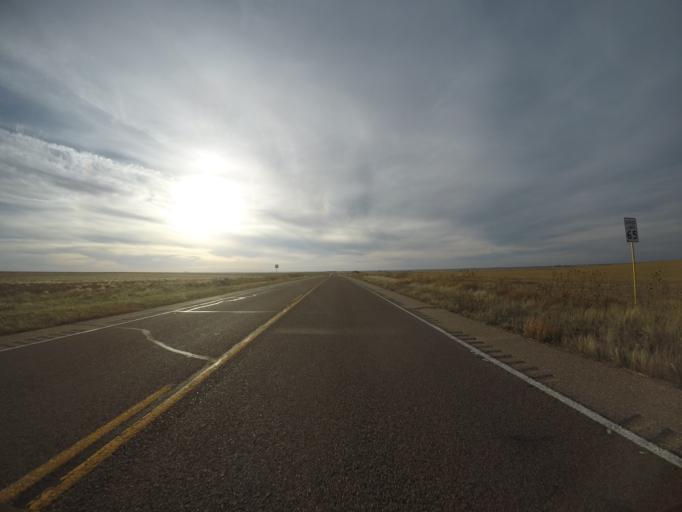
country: US
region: Colorado
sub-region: Kit Carson County
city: Burlington
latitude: 39.6579
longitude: -102.4945
